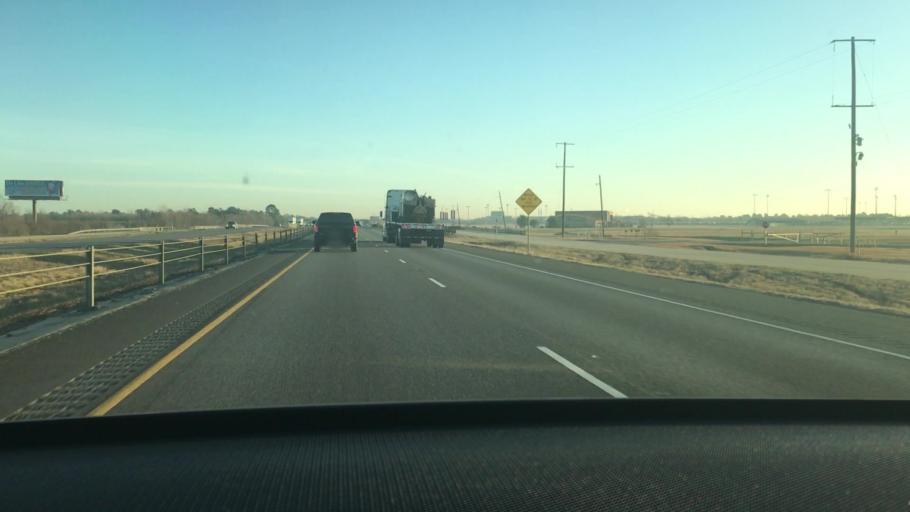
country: US
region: Texas
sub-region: Jefferson County
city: Beaumont
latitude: 30.0131
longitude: -94.1828
